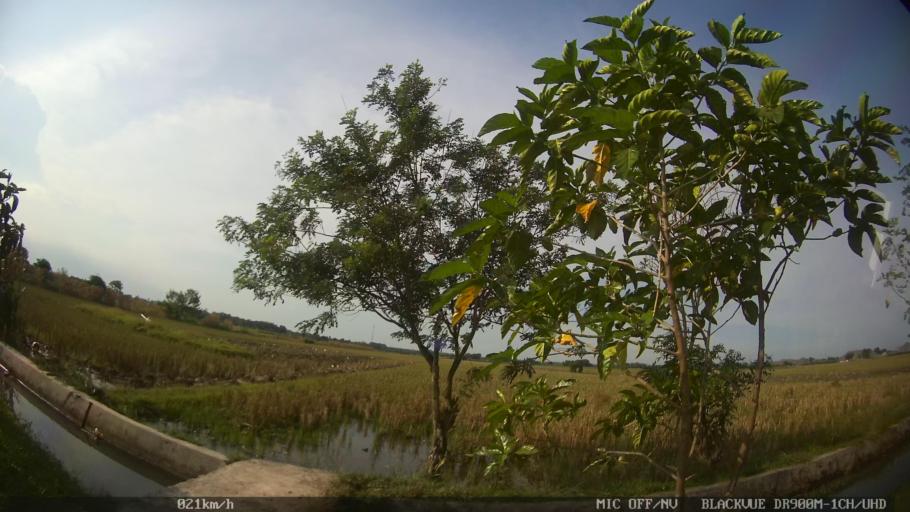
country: ID
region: North Sumatra
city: Binjai
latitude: 3.6211
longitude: 98.5271
